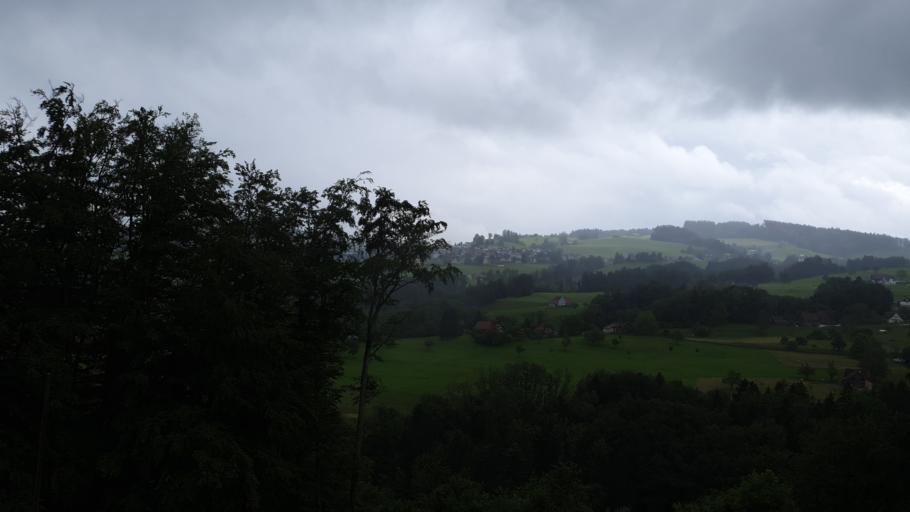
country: CH
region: Appenzell Ausserrhoden
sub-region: Bezirk Vorderland
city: Heiden
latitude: 47.4641
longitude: 9.5383
